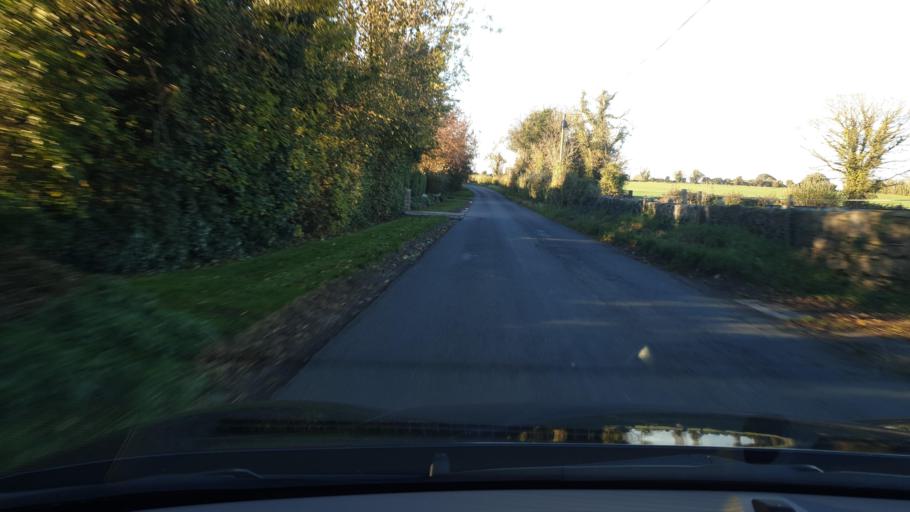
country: IE
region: Leinster
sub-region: Lu
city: Drogheda
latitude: 53.6844
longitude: -6.3330
